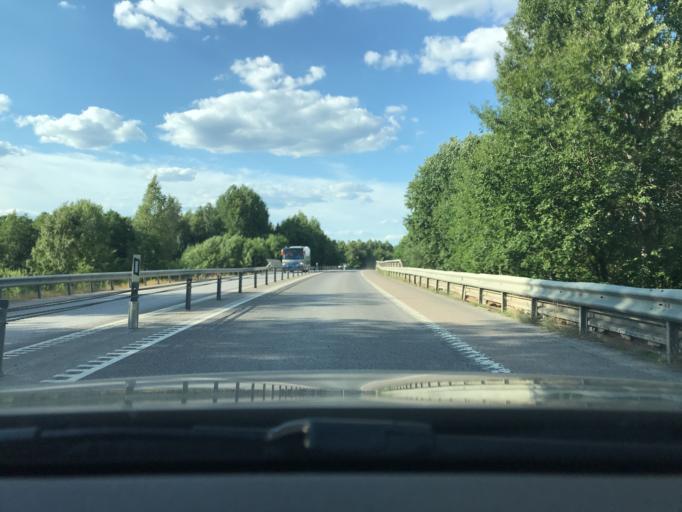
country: SE
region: Kronoberg
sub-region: Vaxjo Kommun
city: Vaexjoe
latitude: 56.8830
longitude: 14.7460
